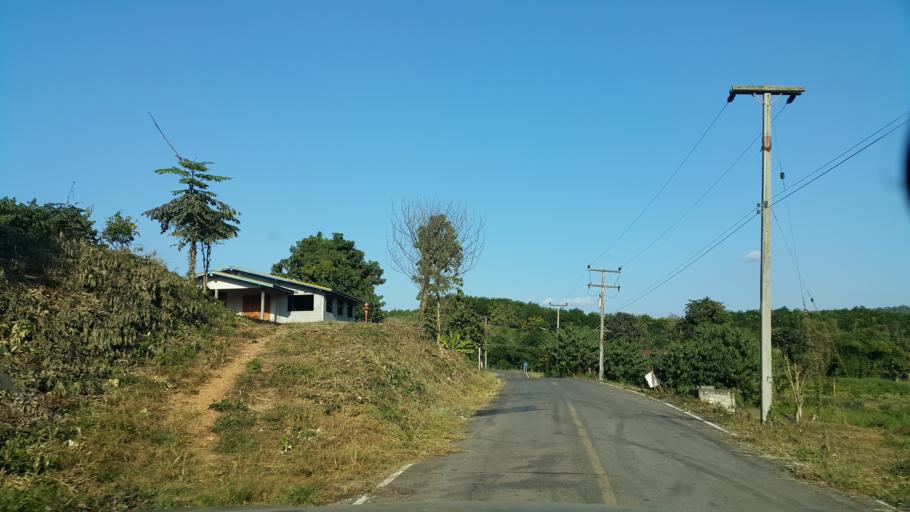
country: TH
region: Sukhothai
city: Thung Saliam
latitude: 17.4010
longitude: 99.5120
